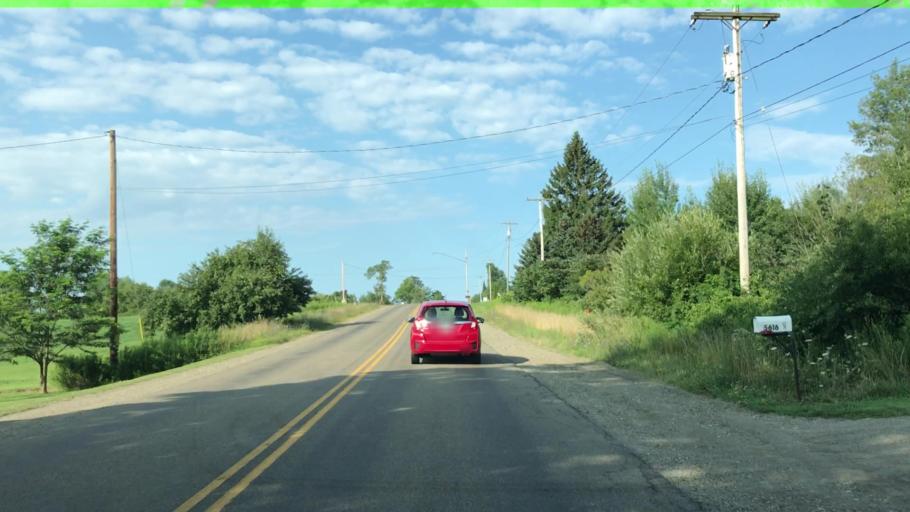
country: US
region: New York
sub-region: Chautauqua County
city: Mayville
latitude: 42.2882
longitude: -79.4260
